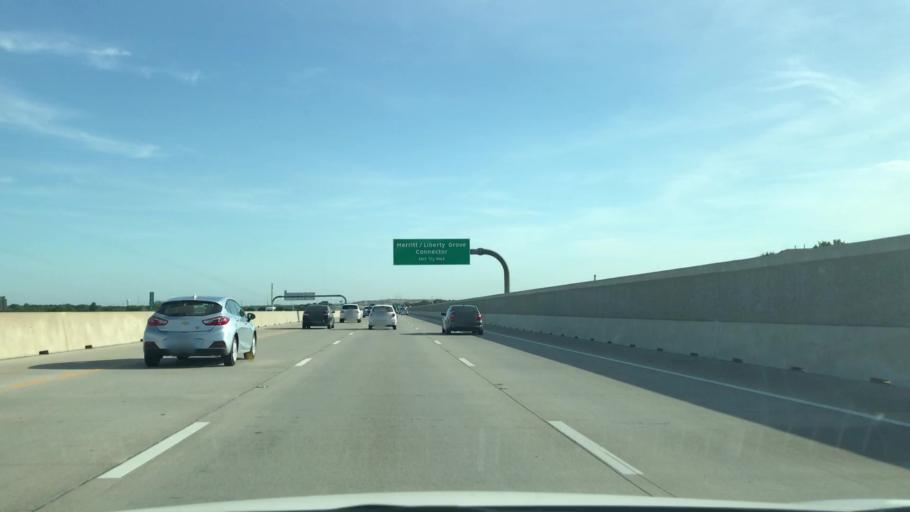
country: US
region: Texas
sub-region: Dallas County
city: Rowlett
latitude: 32.9185
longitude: -96.5542
